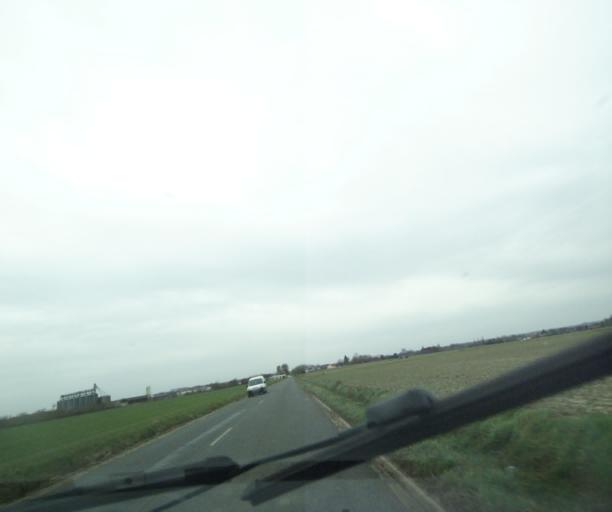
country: FR
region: Nord-Pas-de-Calais
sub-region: Departement du Nord
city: Quarouble
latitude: 50.3757
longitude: 3.6330
